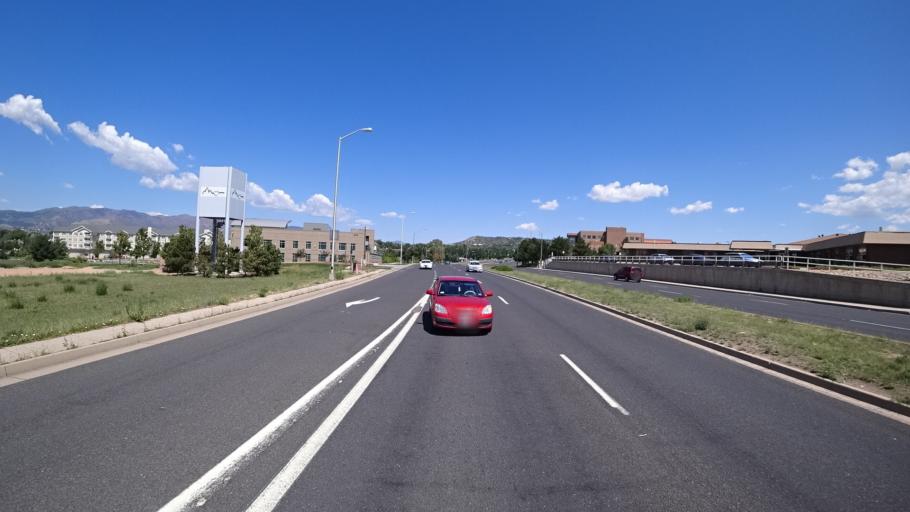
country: US
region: Colorado
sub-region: El Paso County
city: Colorado Springs
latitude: 38.8711
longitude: -104.7945
